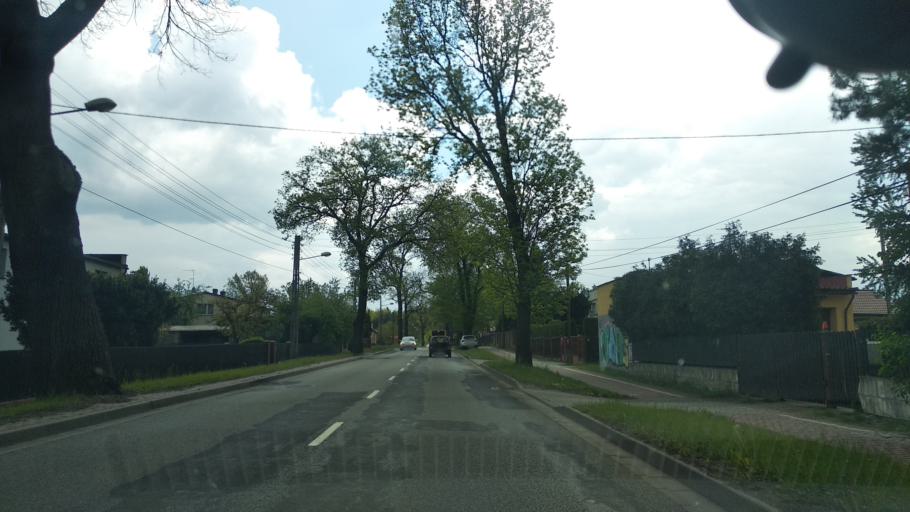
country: PL
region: Silesian Voivodeship
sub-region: Powiat mikolowski
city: Mikolow
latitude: 50.2255
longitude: 18.9245
